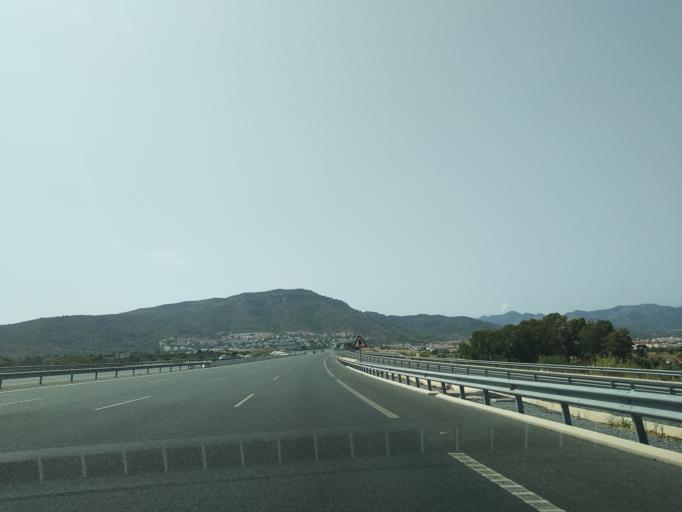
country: ES
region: Andalusia
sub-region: Provincia de Malaga
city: Alhaurin de la Torre
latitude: 36.6748
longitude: -4.5270
